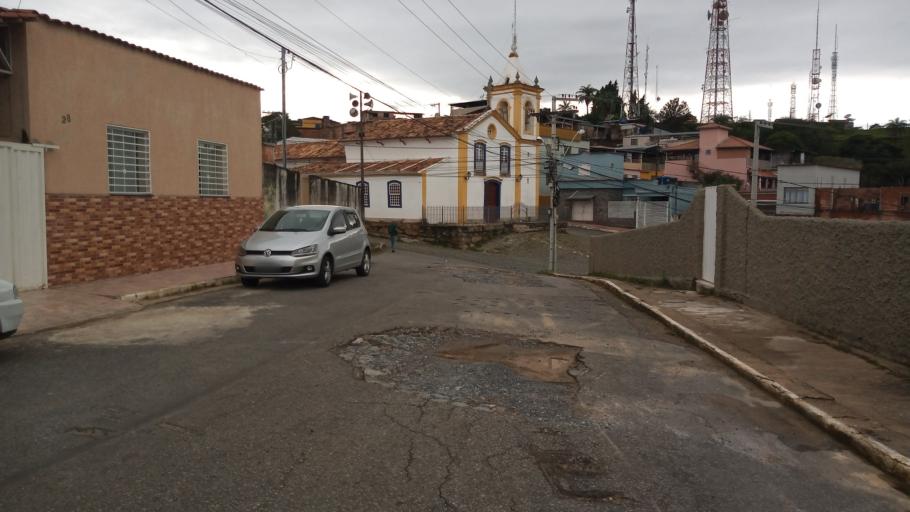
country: BR
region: Minas Gerais
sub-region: Sao Joao Del Rei
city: Sao Joao del Rei
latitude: -21.1276
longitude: -44.2646
